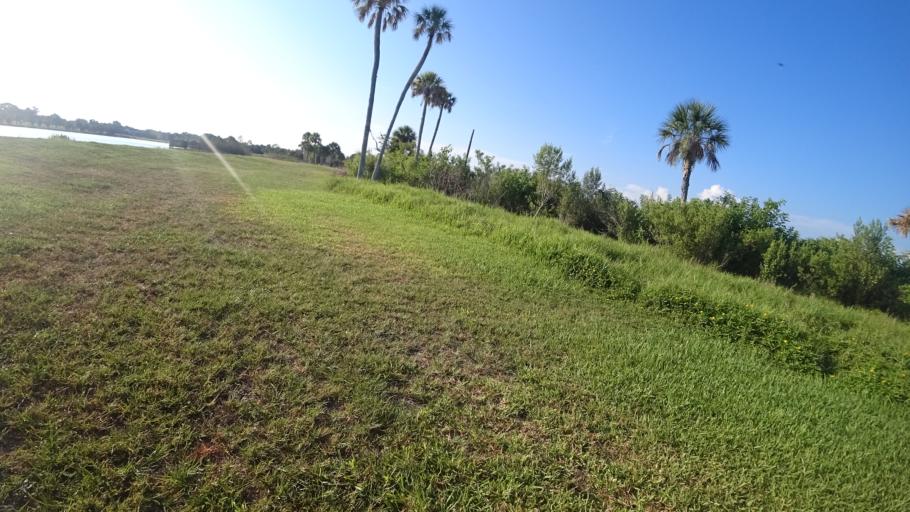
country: US
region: Florida
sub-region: Manatee County
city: Ellenton
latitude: 27.5028
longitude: -82.4876
